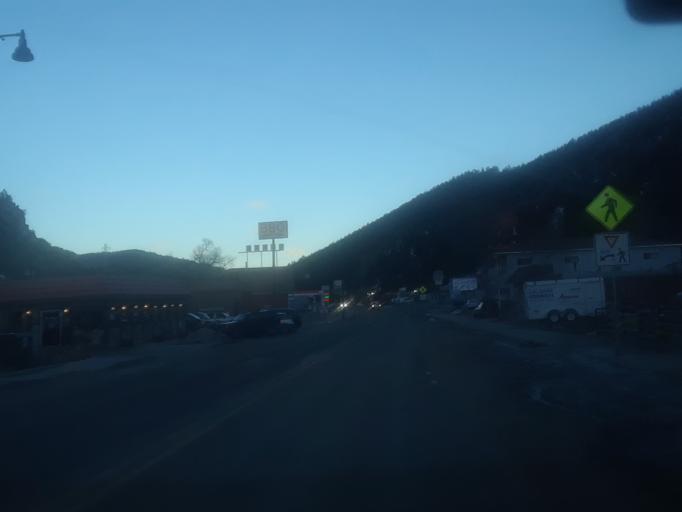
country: US
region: Colorado
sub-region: Clear Creek County
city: Idaho Springs
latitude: 39.7416
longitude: -105.5020
